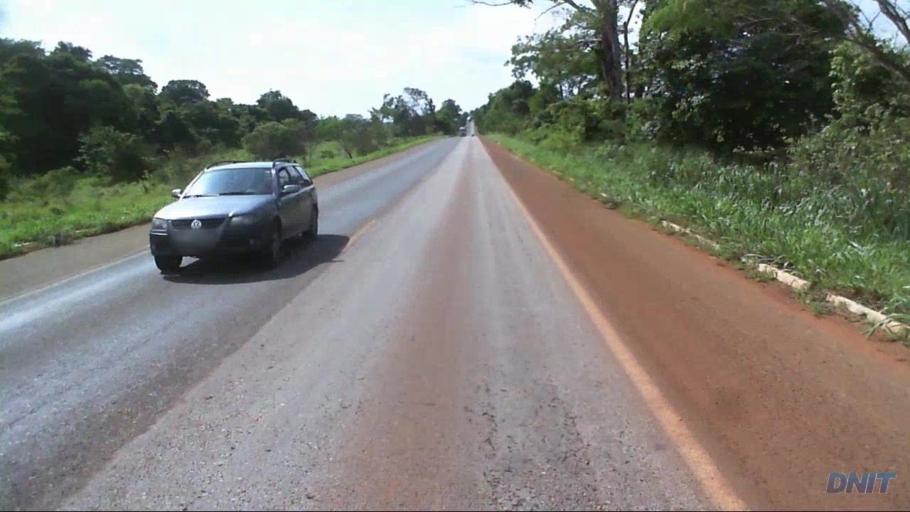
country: BR
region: Goias
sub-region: Barro Alto
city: Barro Alto
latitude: -15.0094
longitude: -48.9016
